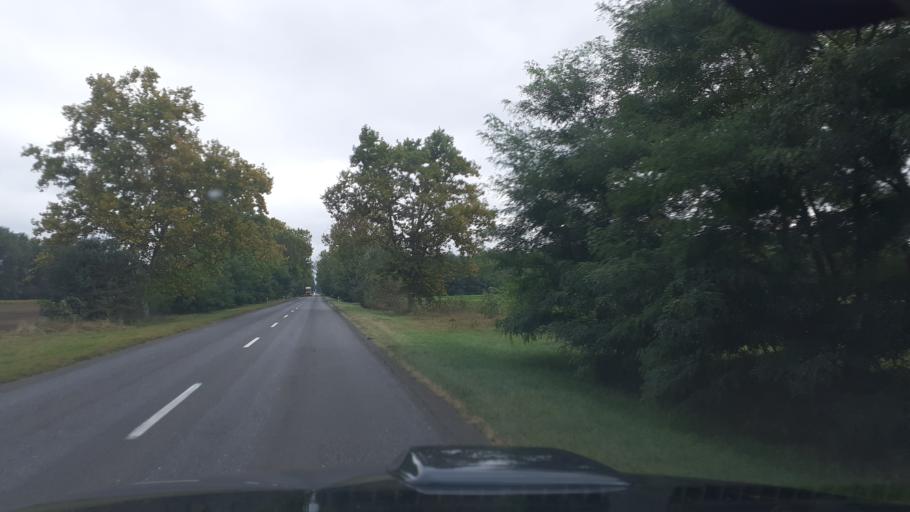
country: HU
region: Bacs-Kiskun
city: Balloszog
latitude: 46.8829
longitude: 19.5261
